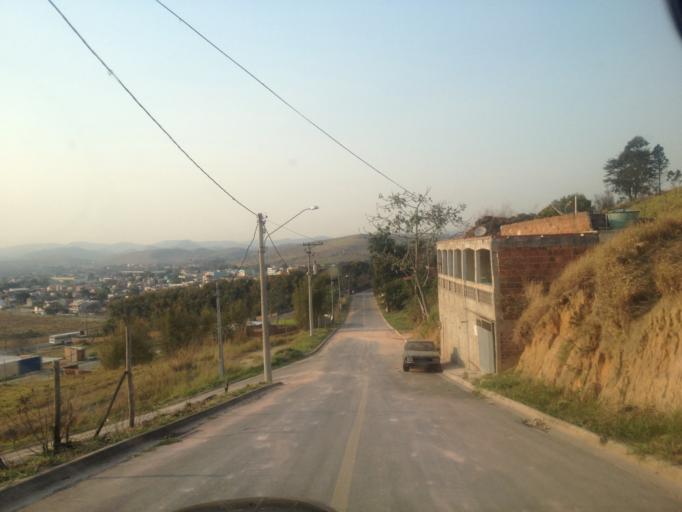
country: BR
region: Rio de Janeiro
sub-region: Porto Real
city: Porto Real
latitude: -22.4350
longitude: -44.3185
